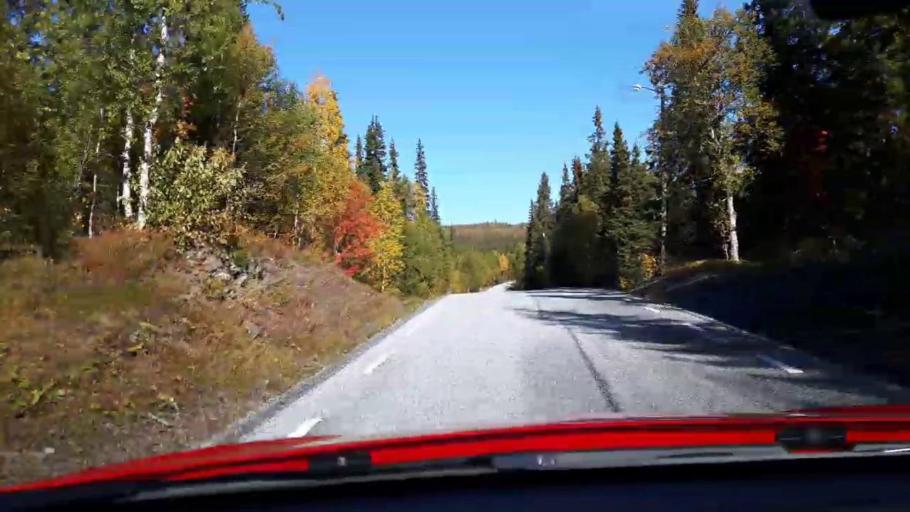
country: NO
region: Nord-Trondelag
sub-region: Royrvik
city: Royrvik
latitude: 64.8126
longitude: 14.1739
